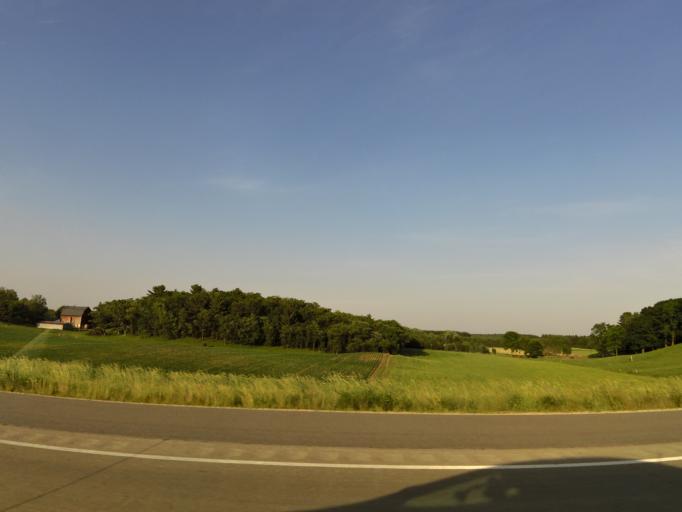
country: US
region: Wisconsin
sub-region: Monroe County
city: Tomah
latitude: 44.0442
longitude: -90.5137
